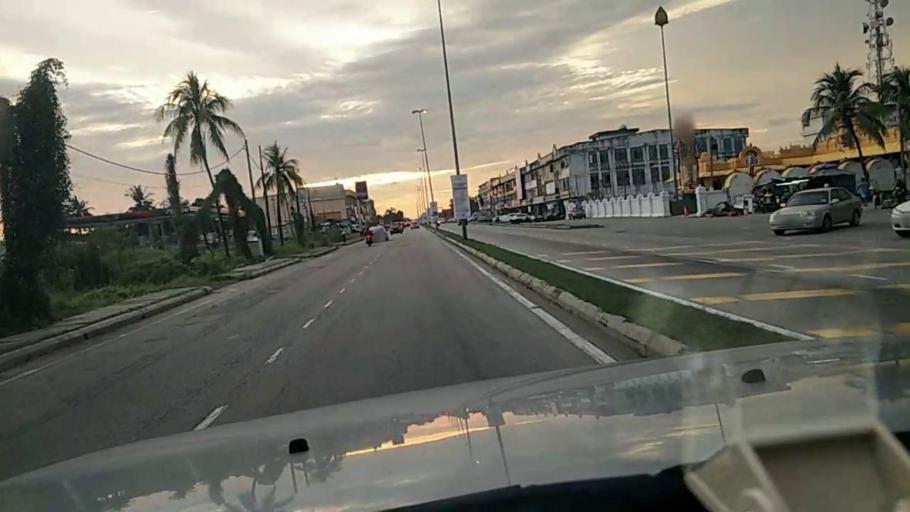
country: MY
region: Perak
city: Kampong Dungun
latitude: 3.1387
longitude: 101.3699
